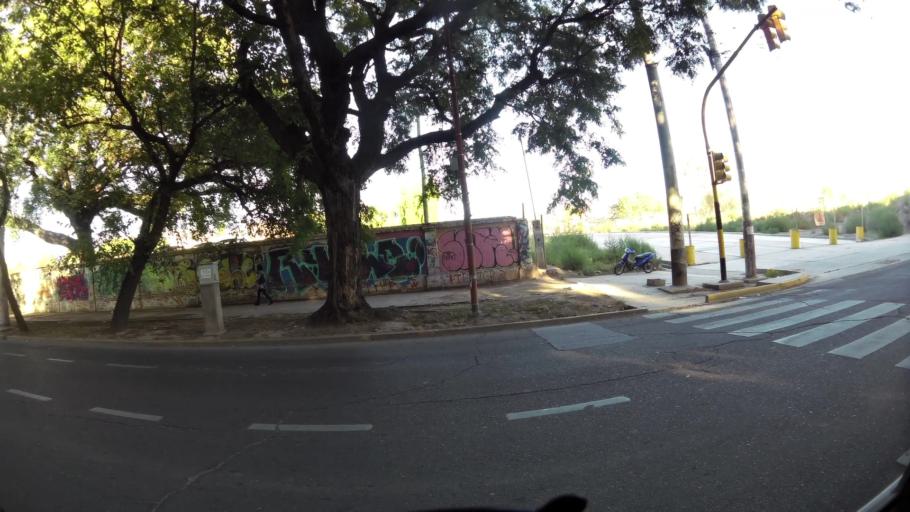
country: AR
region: Mendoza
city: Mendoza
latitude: -32.8826
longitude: -68.8467
